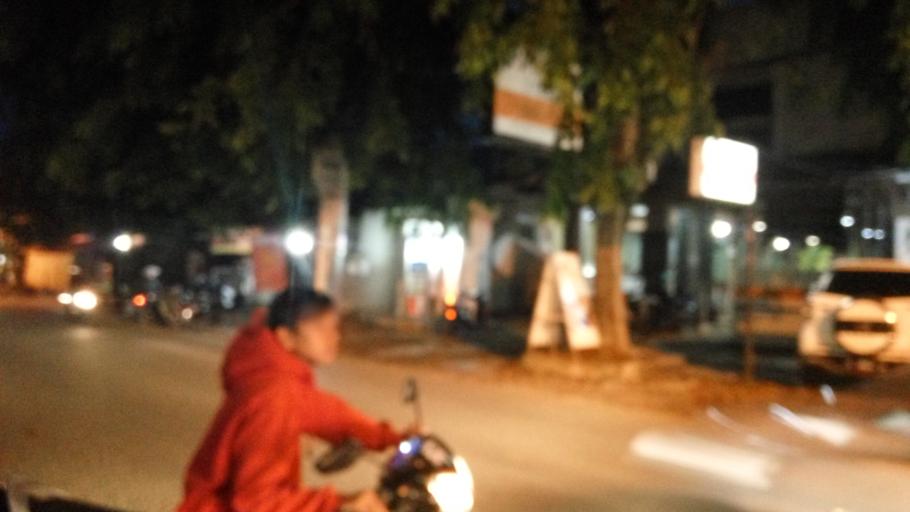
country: ID
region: Central Java
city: Semarang
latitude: -7.0561
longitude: 110.4362
